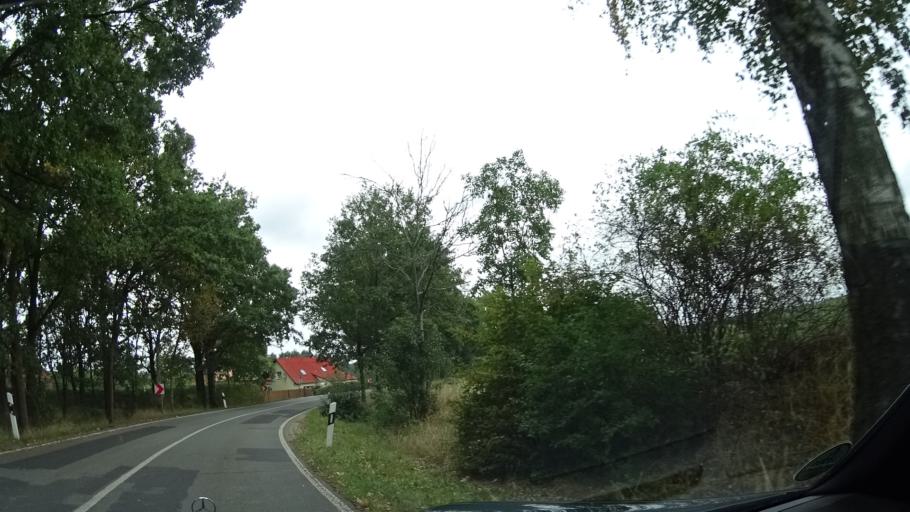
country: DE
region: Brandenburg
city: Walsleben
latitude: 52.9599
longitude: 12.7053
